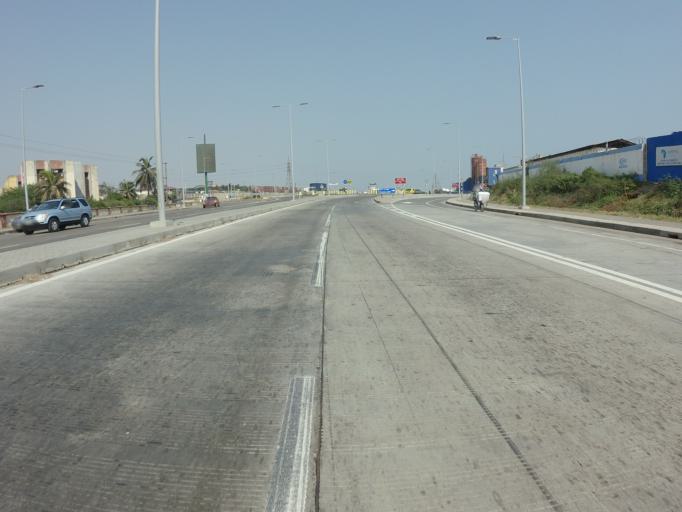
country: GH
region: Greater Accra
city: Tema
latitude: 5.6165
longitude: -0.0239
